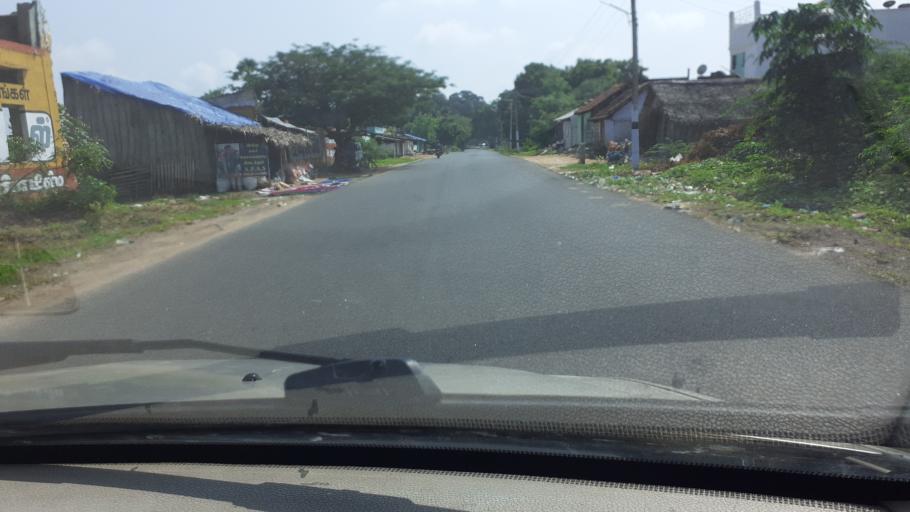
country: IN
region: Tamil Nadu
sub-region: Thoothukkudi
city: Srivaikuntam
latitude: 8.6324
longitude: 77.8999
